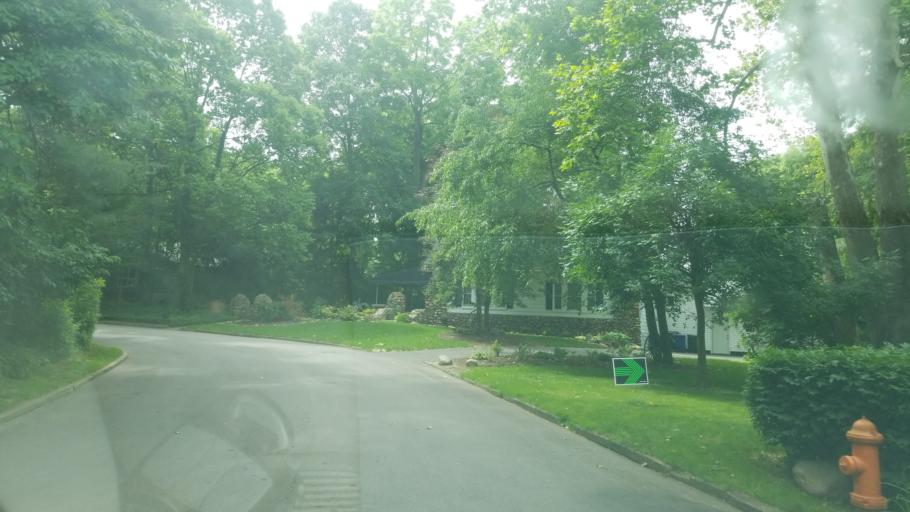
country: US
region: Ohio
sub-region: Franklin County
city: Worthington
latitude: 40.0384
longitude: -83.0254
